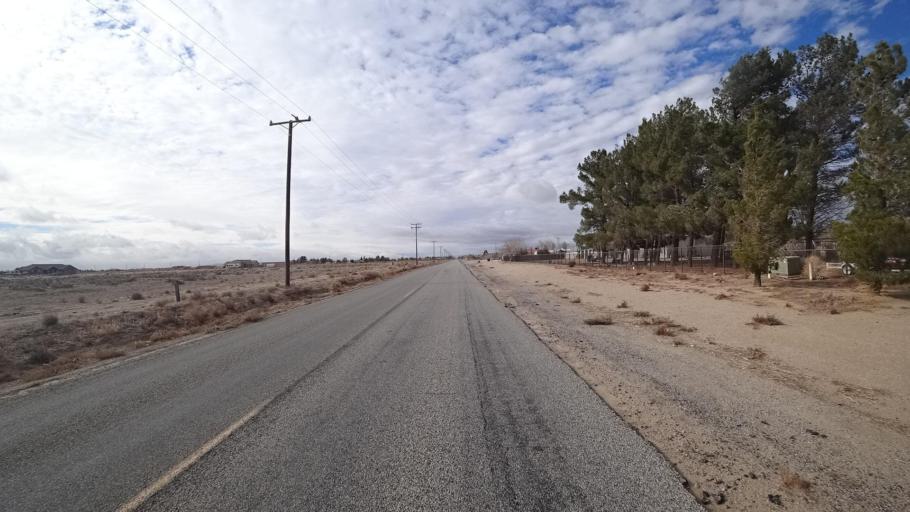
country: US
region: California
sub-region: Kern County
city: Rosamond
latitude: 34.8201
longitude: -118.2474
